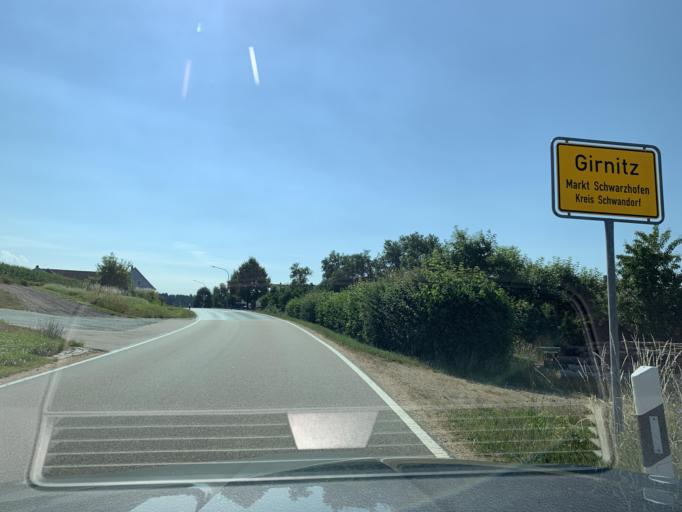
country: DE
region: Bavaria
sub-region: Upper Palatinate
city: Schwarzhofen
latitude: 49.3954
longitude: 12.3234
